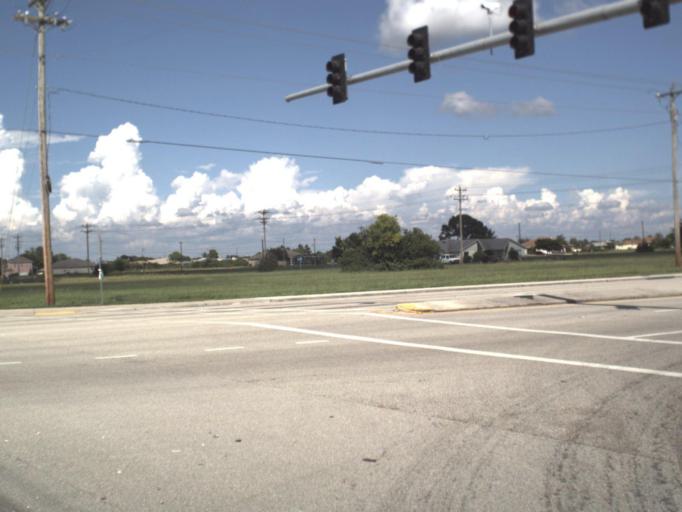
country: US
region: Florida
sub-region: Lee County
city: Palmona Park
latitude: 26.6825
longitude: -81.9417
